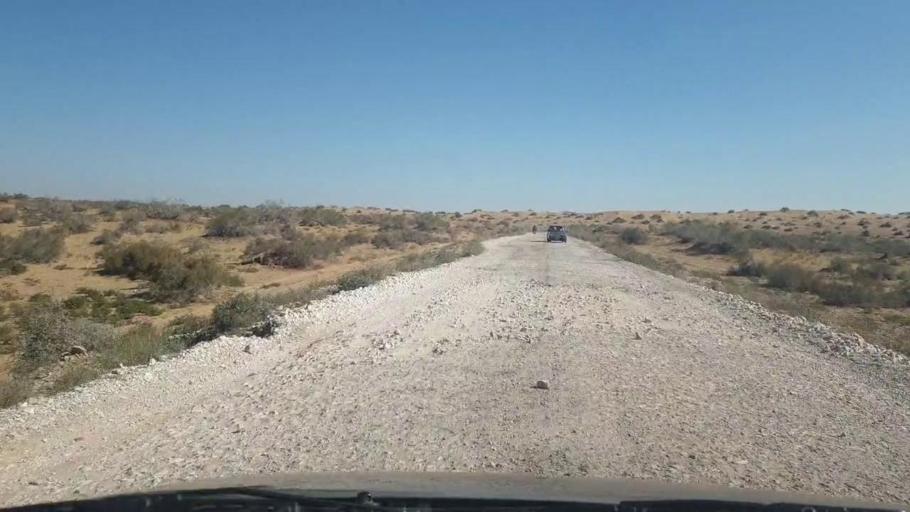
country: PK
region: Sindh
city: Bozdar
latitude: 27.0000
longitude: 68.8312
